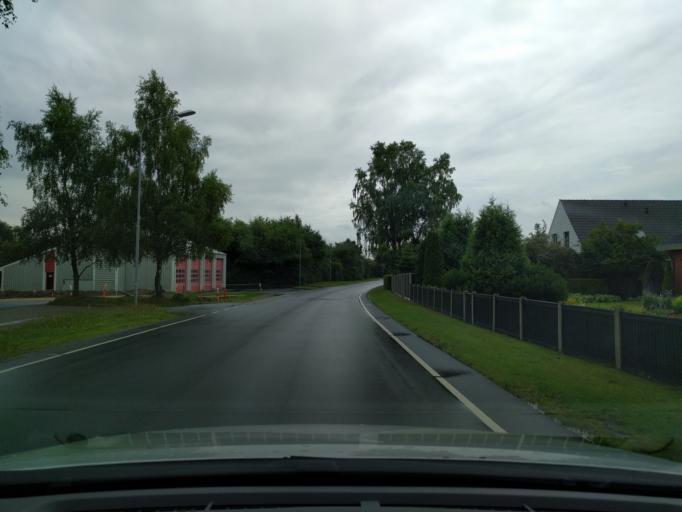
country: DK
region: Central Jutland
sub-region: Skanderborg Kommune
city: Ry
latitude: 56.0875
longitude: 9.7784
